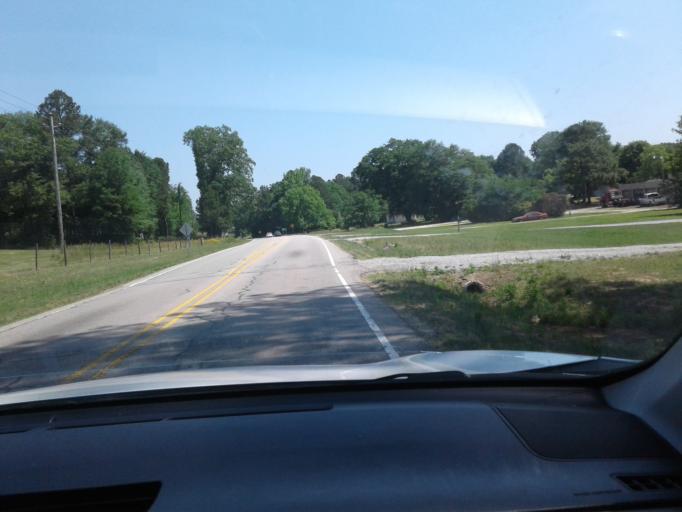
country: US
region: North Carolina
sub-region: Wake County
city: Holly Springs
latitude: 35.6240
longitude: -78.8411
